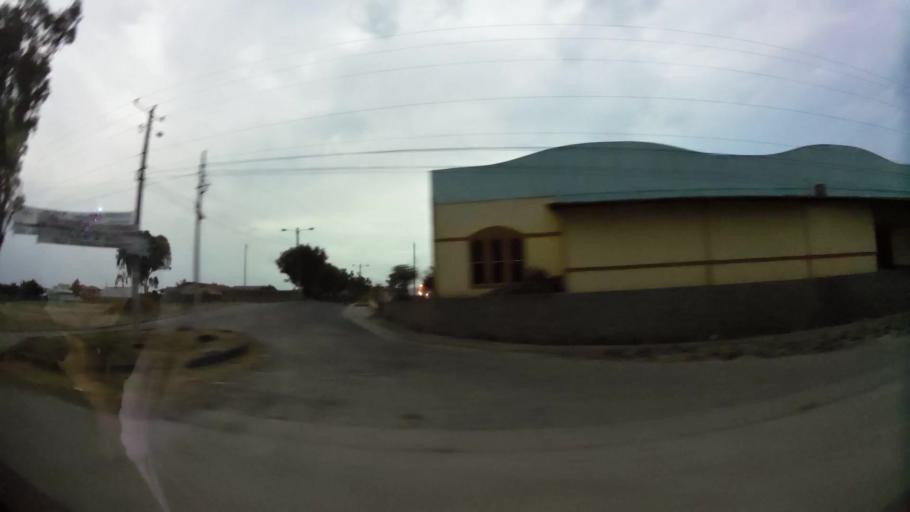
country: NI
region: Esteli
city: Esteli
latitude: 13.1049
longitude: -86.3546
